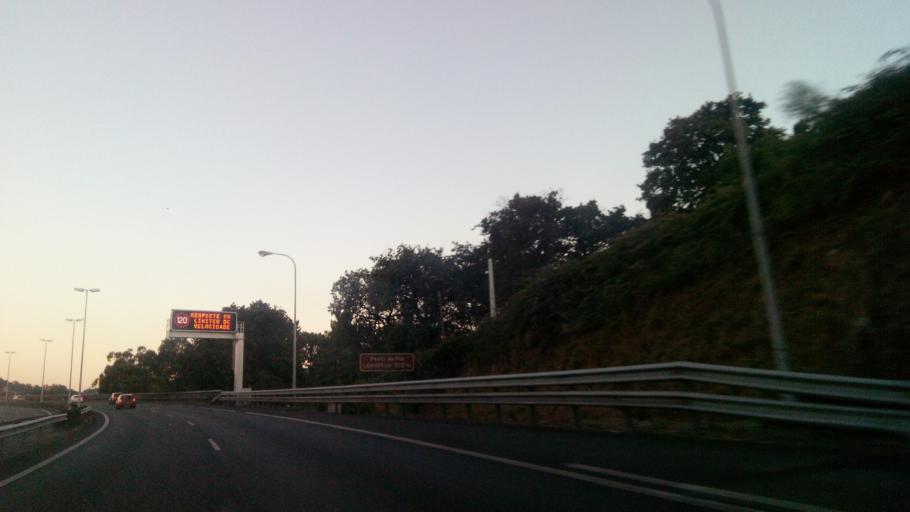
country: ES
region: Galicia
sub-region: Provincia de Pontevedra
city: Poio
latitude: 42.4294
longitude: -8.6564
